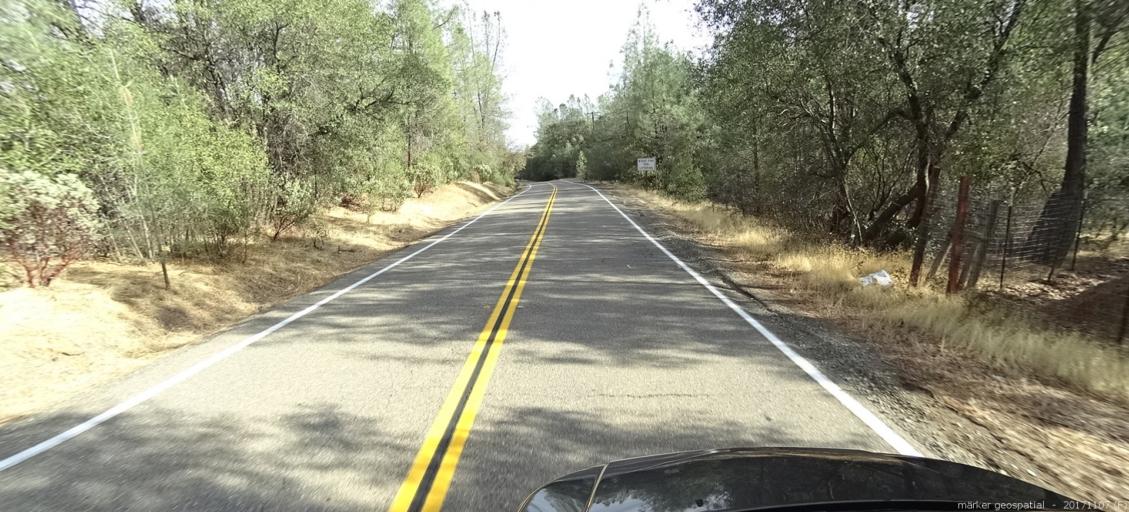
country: US
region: California
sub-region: Shasta County
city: Shasta
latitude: 40.5198
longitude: -122.4963
